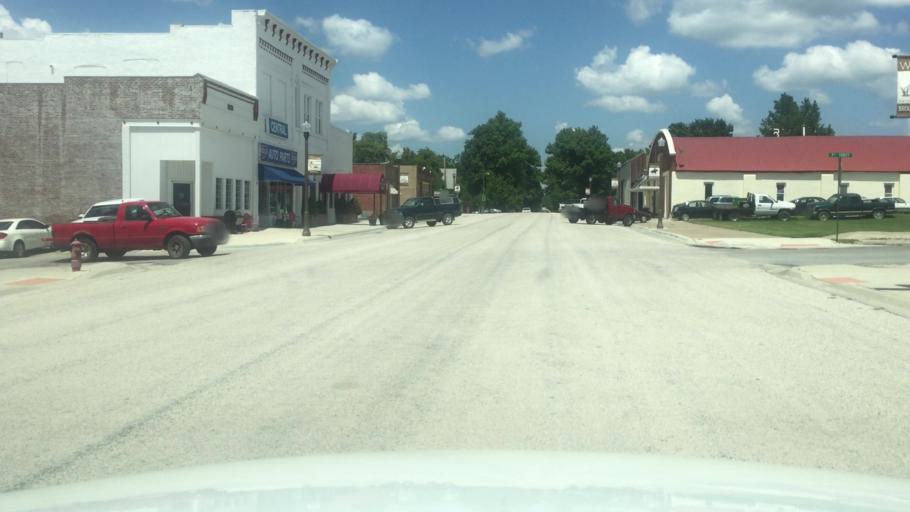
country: US
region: Kansas
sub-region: Brown County
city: Horton
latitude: 39.6608
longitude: -95.5274
